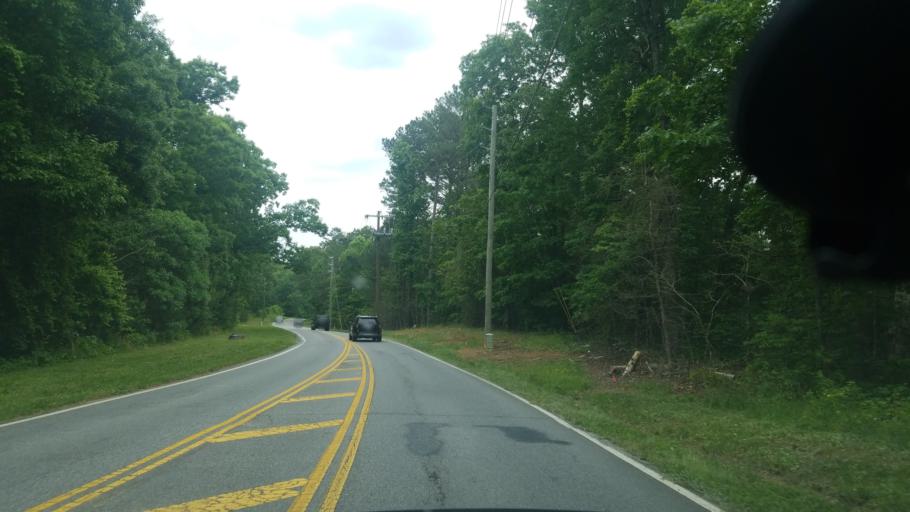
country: US
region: Georgia
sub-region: Forsyth County
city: Cumming
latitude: 34.1715
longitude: -84.1332
